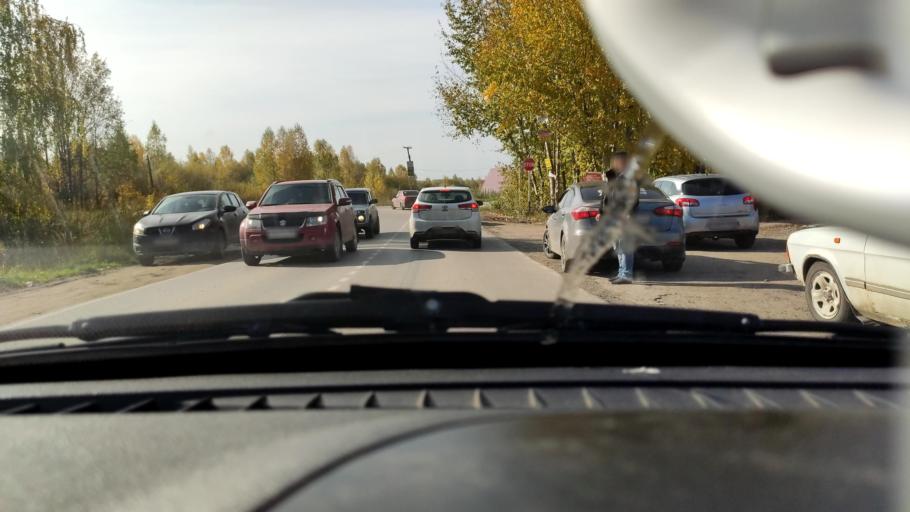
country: RU
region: Perm
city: Overyata
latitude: 58.0560
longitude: 55.8787
